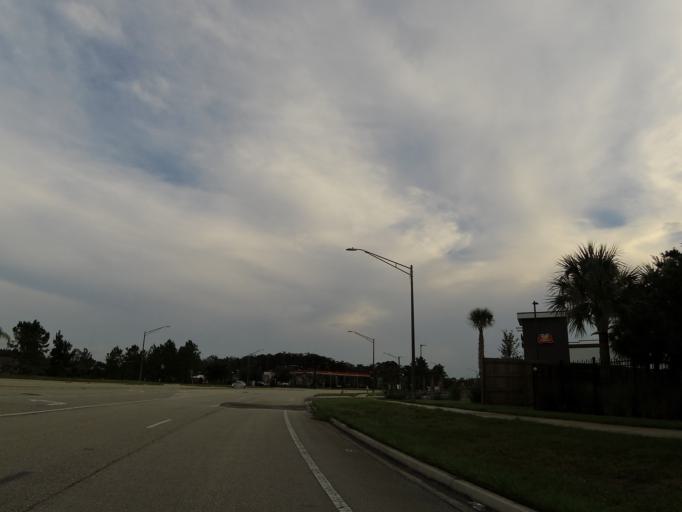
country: US
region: Florida
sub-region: Saint Johns County
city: Ponte Vedra Beach
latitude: 30.2186
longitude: -81.5095
